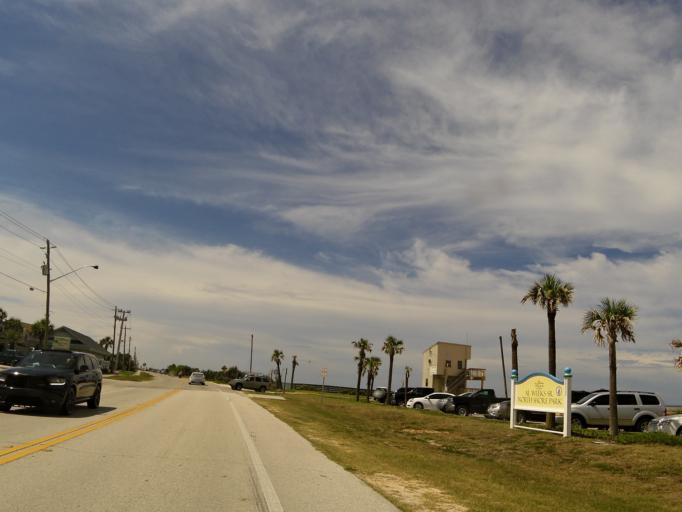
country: US
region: Florida
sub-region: Volusia County
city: Ormond-by-the-Sea
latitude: 29.3335
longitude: -81.0592
